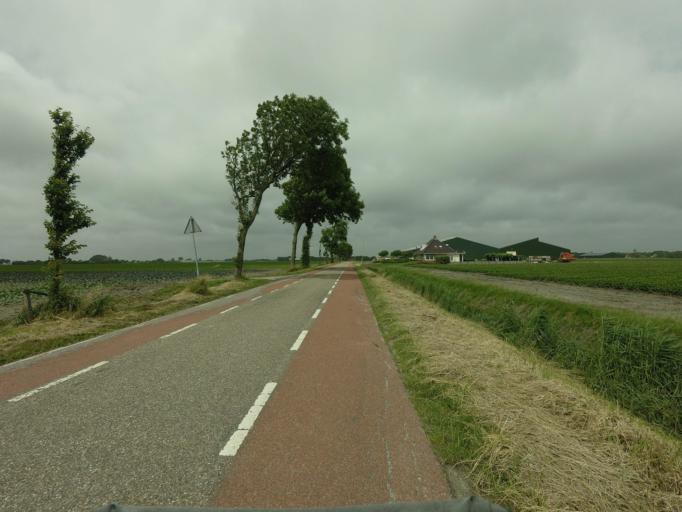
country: NL
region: North Holland
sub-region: Gemeente Schagen
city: Harenkarspel
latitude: 52.7453
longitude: 4.7560
